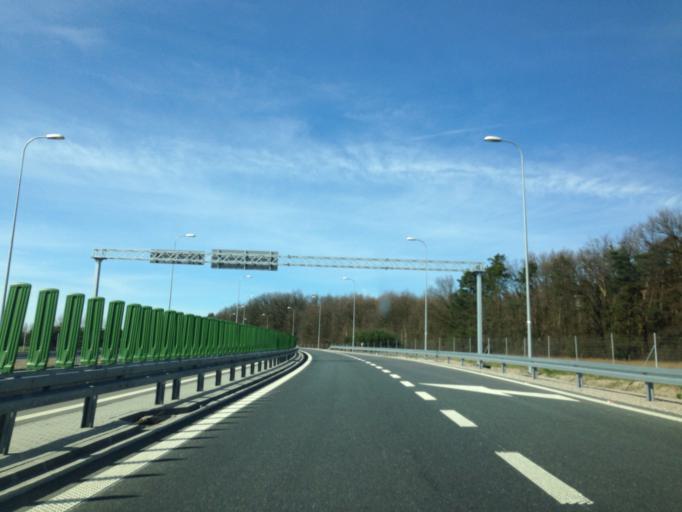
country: PL
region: Lodz Voivodeship
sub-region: Powiat zdunskowolski
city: Zapolice
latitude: 51.5952
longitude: 18.8225
